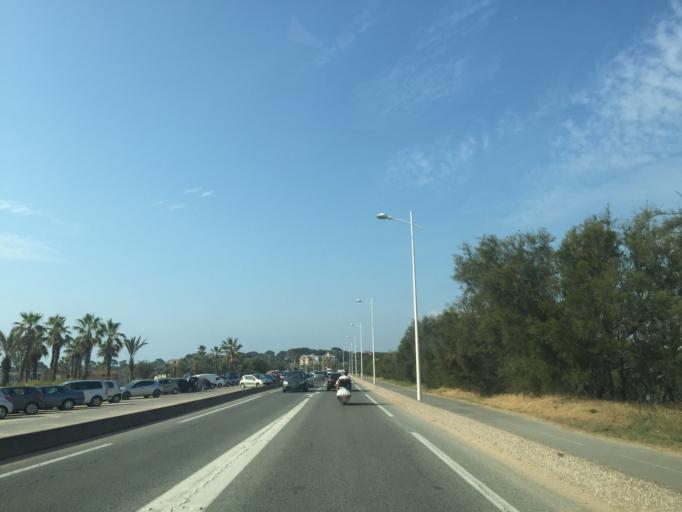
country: FR
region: Provence-Alpes-Cote d'Azur
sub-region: Departement du Var
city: Frejus
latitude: 43.3978
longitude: 6.7293
